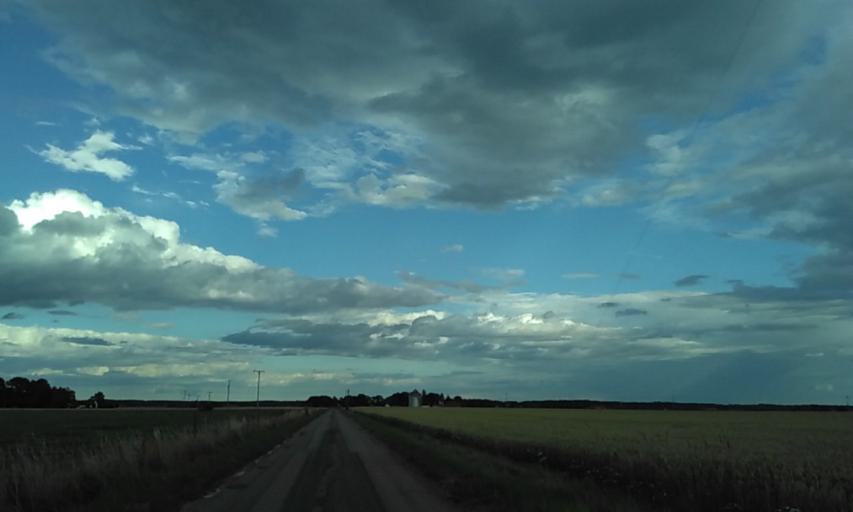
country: SE
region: Vaestra Goetaland
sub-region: Grastorps Kommun
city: Graestorp
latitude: 58.4098
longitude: 12.7225
